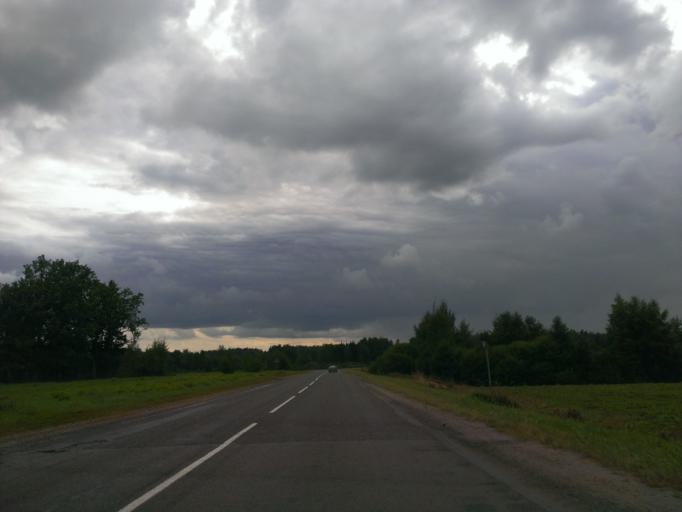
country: LV
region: Kegums
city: Kegums
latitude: 56.7702
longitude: 24.7705
